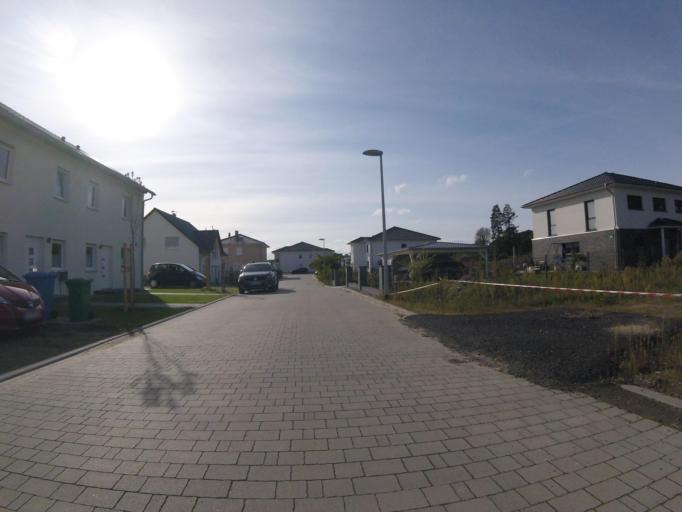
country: DE
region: Brandenburg
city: Konigs Wusterhausen
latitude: 52.2967
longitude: 13.6886
